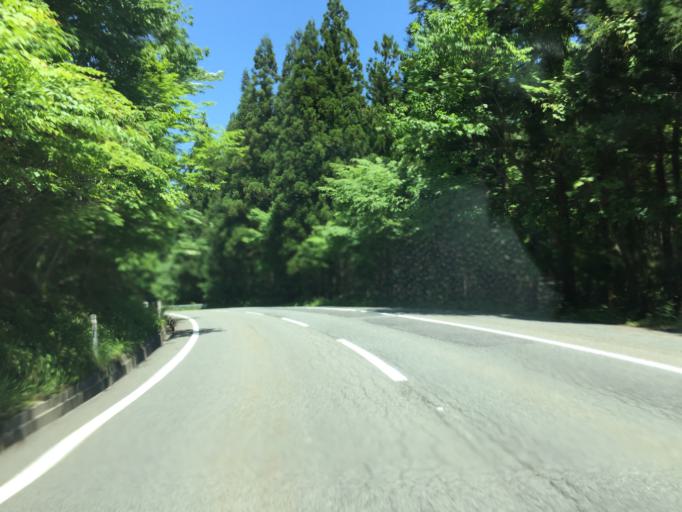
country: JP
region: Fukushima
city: Namie
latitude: 37.5212
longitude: 140.7985
